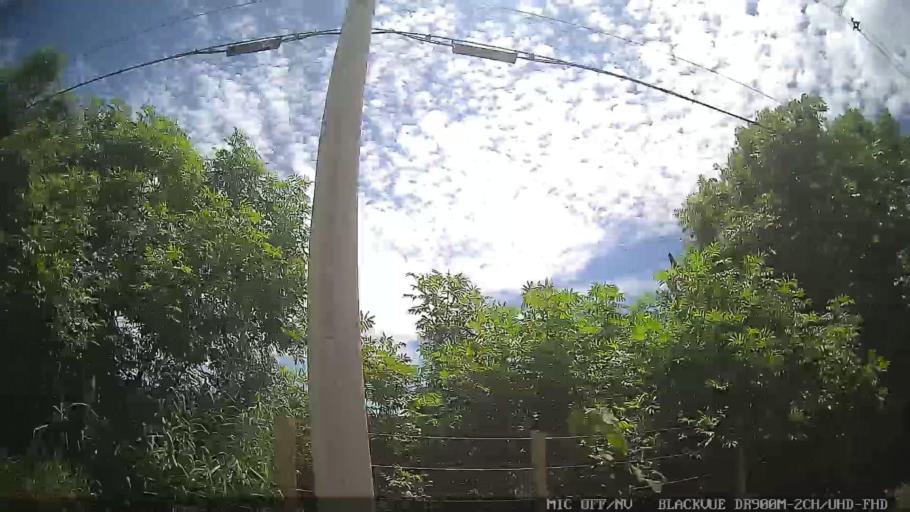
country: BR
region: Sao Paulo
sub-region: Biritiba-Mirim
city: Biritiba Mirim
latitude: -23.6053
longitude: -46.0518
